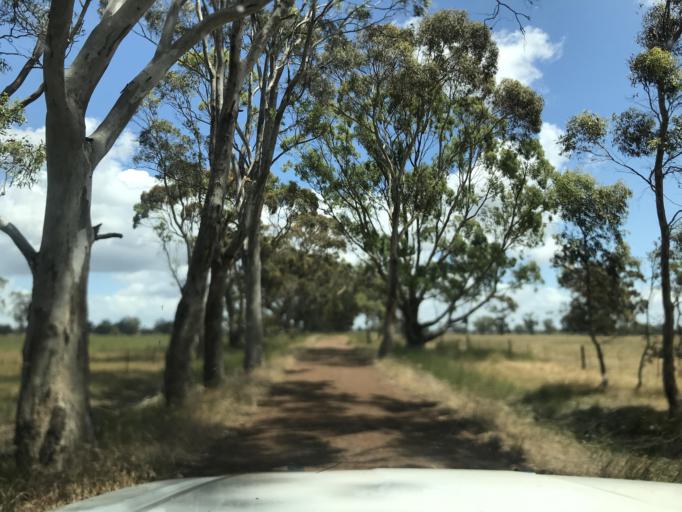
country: AU
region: South Australia
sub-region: Wattle Range
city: Penola
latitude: -37.0748
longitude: 141.3362
